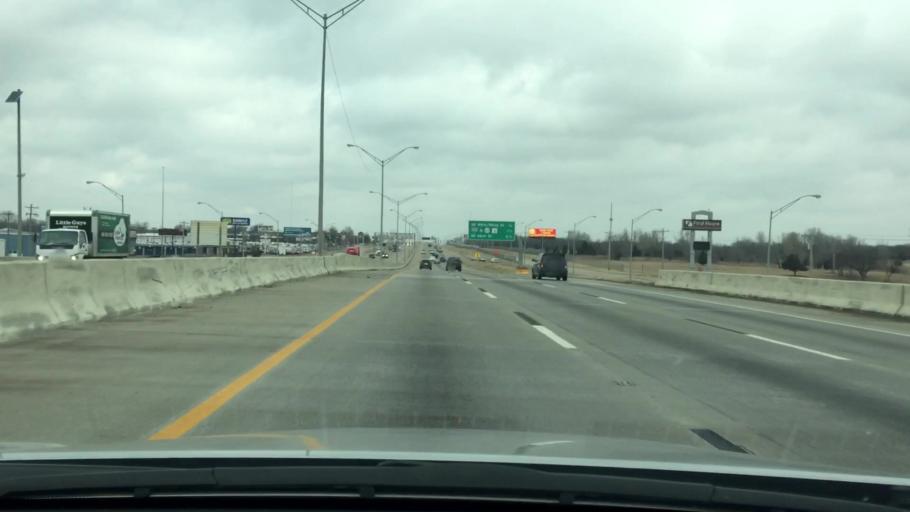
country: US
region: Oklahoma
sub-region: Cleveland County
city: Moore
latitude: 35.3635
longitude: -97.4948
